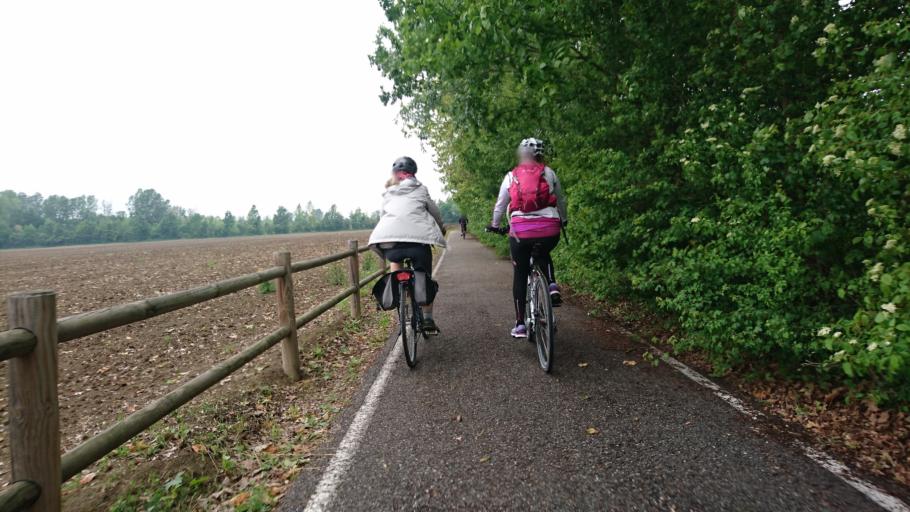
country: IT
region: Veneto
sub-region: Provincia di Padova
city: Montemerlo
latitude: 45.3775
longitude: 11.6900
